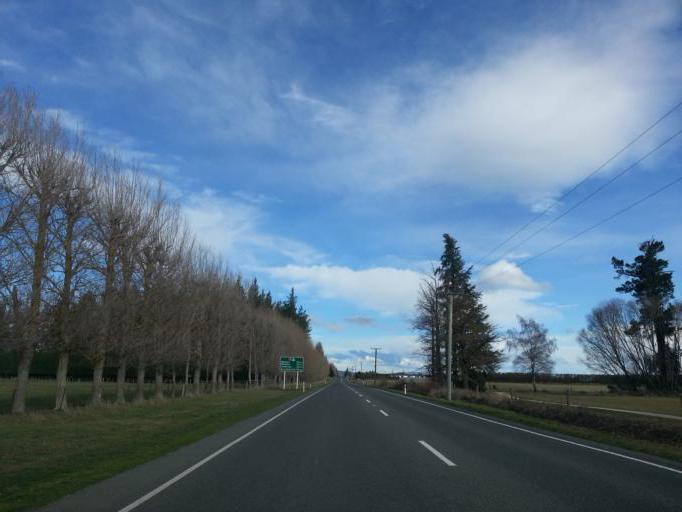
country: NZ
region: Canterbury
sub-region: Hurunui District
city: Amberley
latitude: -42.7775
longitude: 172.8454
